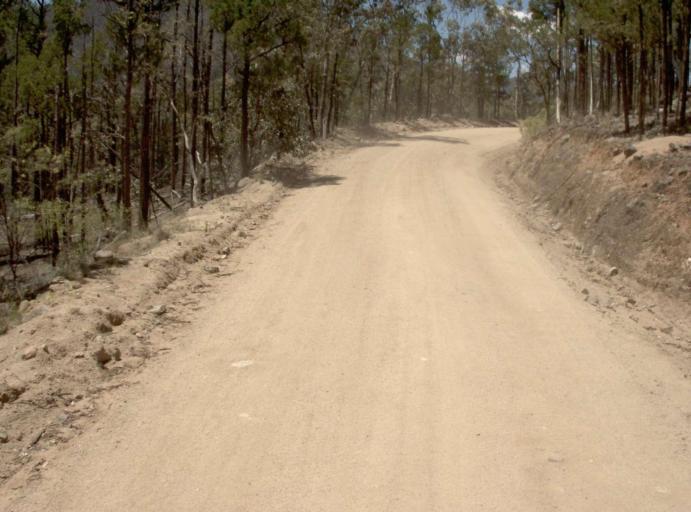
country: AU
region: New South Wales
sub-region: Snowy River
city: Jindabyne
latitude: -36.9045
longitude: 148.4164
